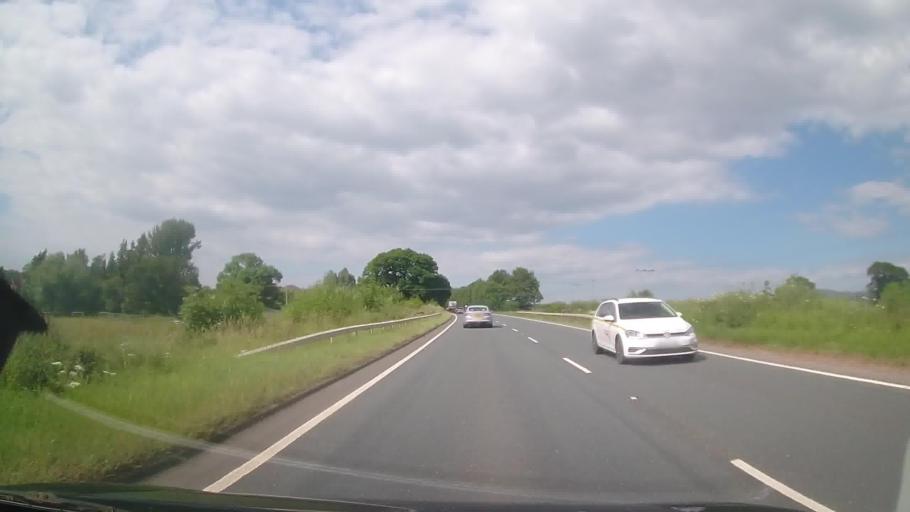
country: GB
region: England
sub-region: Shropshire
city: Ludlow
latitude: 52.3603
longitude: -2.6971
